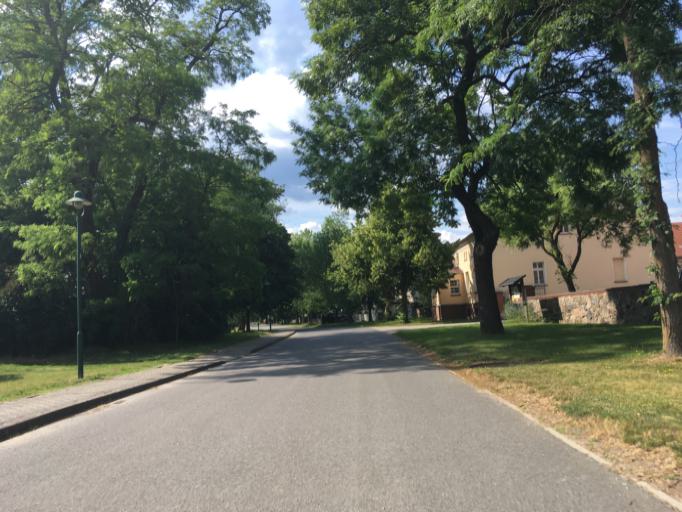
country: DE
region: Brandenburg
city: Steinhofel
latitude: 52.4232
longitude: 14.1150
